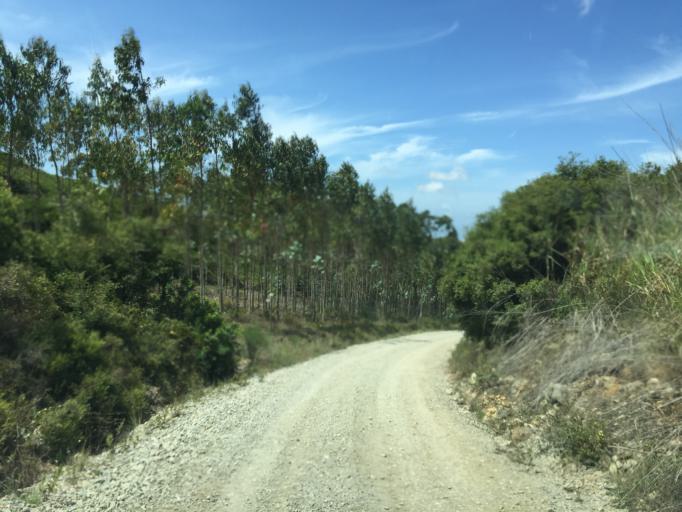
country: PT
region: Leiria
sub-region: Peniche
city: Atouguia da Baleia
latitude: 39.3231
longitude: -9.2619
